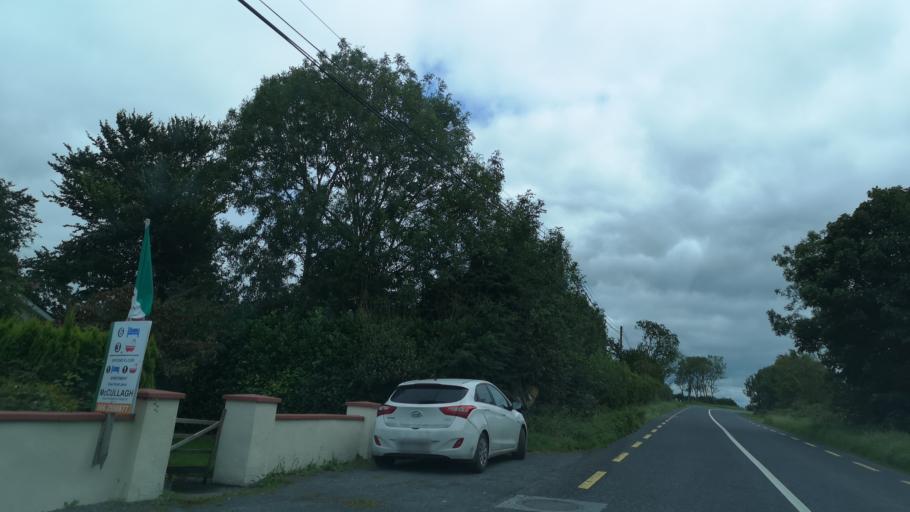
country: IE
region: Connaught
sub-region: County Galway
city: Ballinasloe
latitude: 53.3186
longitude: -8.1748
